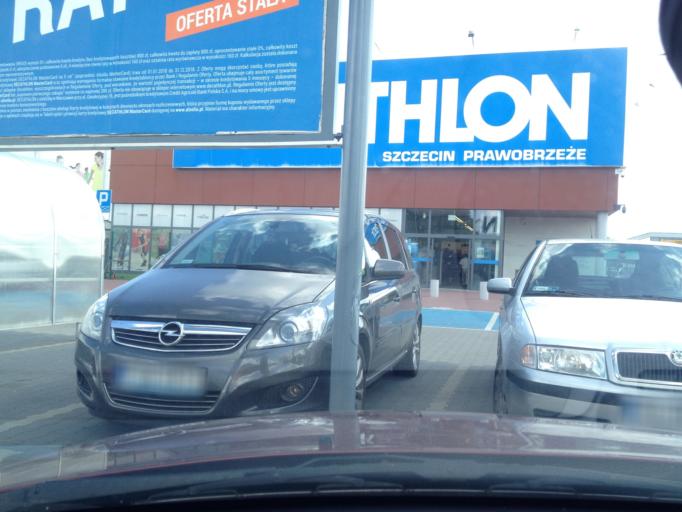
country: PL
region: West Pomeranian Voivodeship
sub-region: Szczecin
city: Szczecin
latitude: 53.3838
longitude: 14.6669
